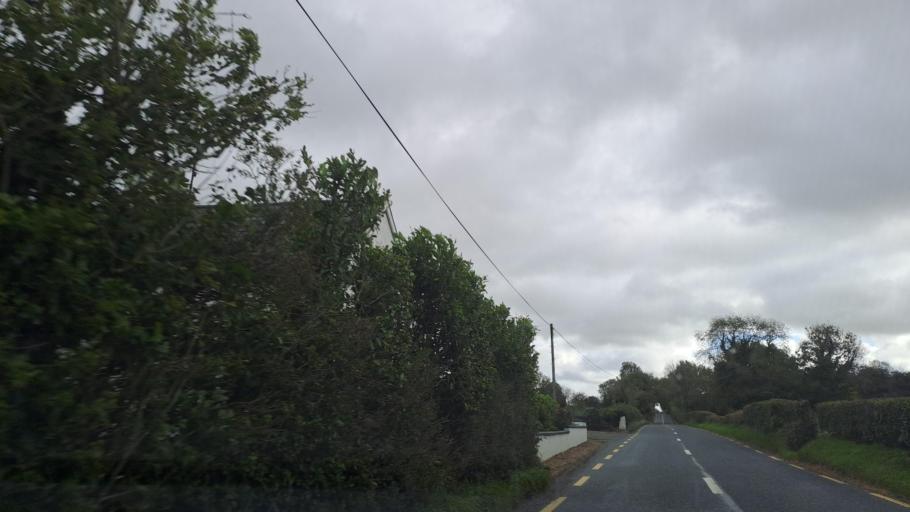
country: IE
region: Ulster
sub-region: An Cabhan
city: Kingscourt
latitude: 53.9161
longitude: -6.8549
